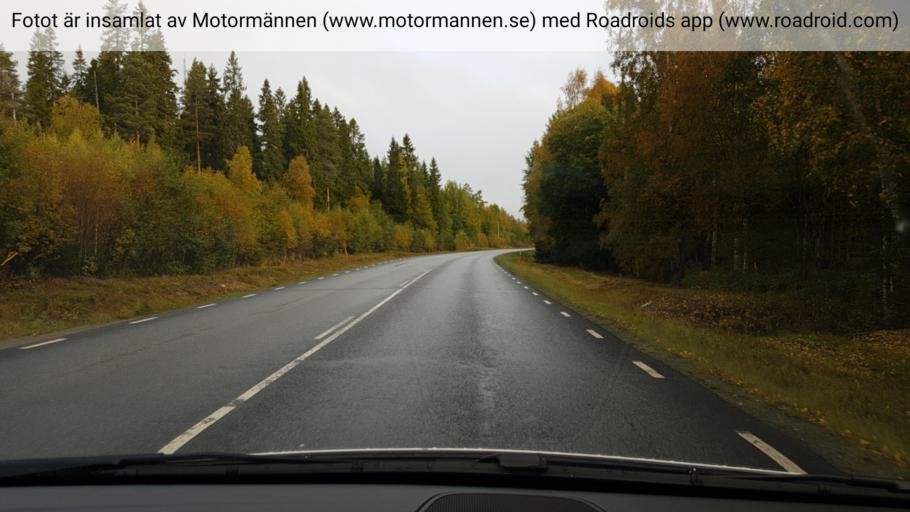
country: SE
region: Vaesterbotten
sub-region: Umea Kommun
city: Ersmark
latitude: 63.8656
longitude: 20.3005
